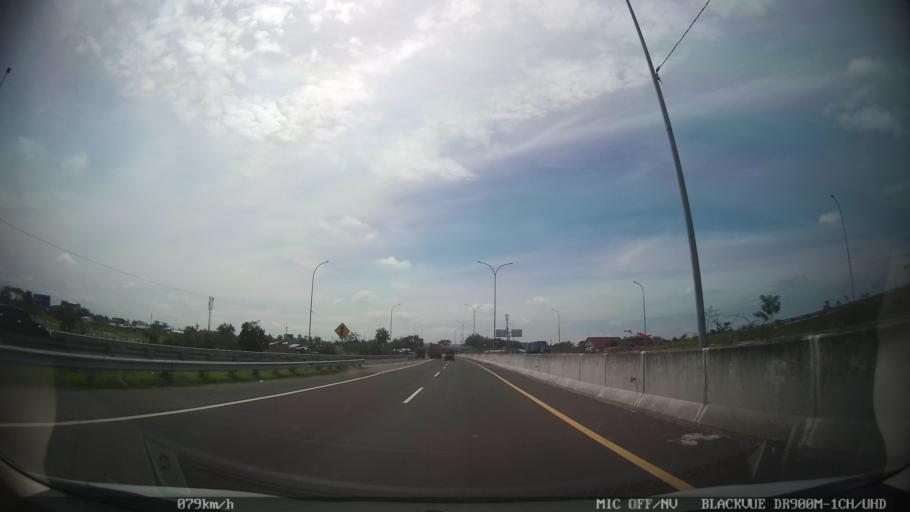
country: ID
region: North Sumatra
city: Medan
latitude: 3.6480
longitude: 98.6843
